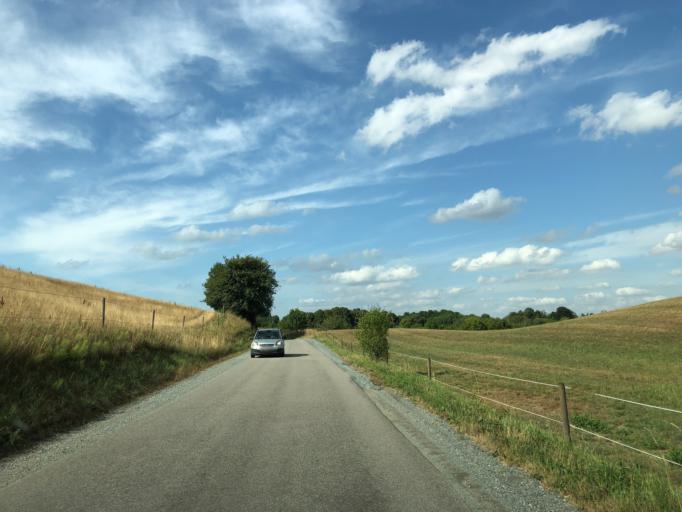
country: DK
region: South Denmark
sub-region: Vejle Kommune
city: Egtved
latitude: 55.6674
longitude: 9.3029
